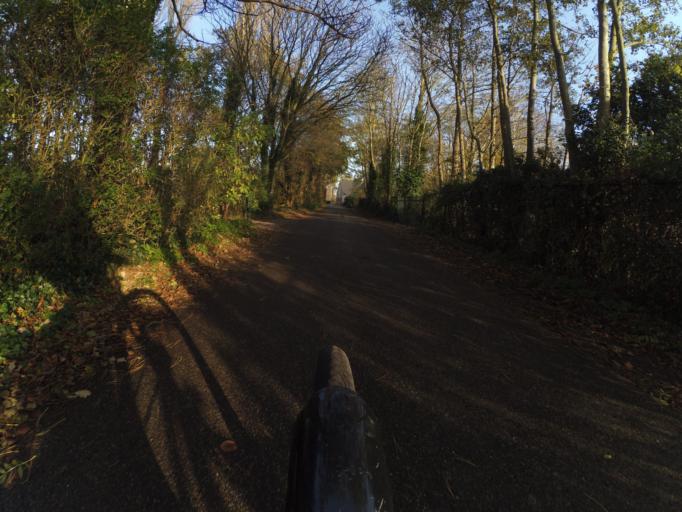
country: NL
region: South Holland
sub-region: Gemeente Goeree-Overflakkee
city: Goedereede
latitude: 51.8296
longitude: 3.9658
